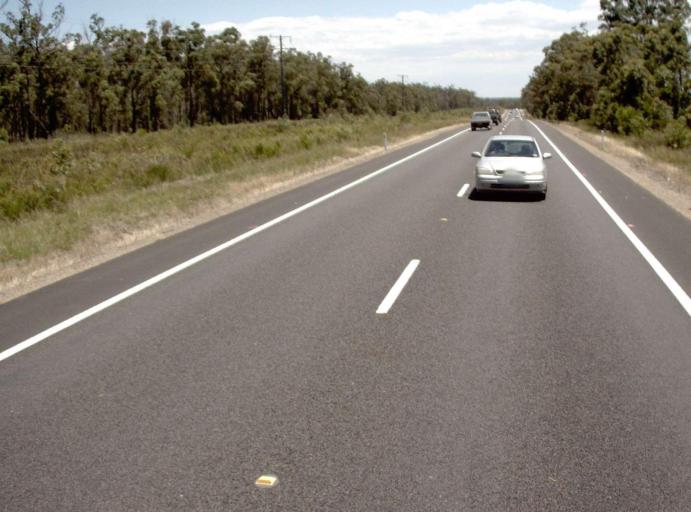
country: AU
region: Victoria
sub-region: East Gippsland
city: Lakes Entrance
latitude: -37.7547
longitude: 148.3151
